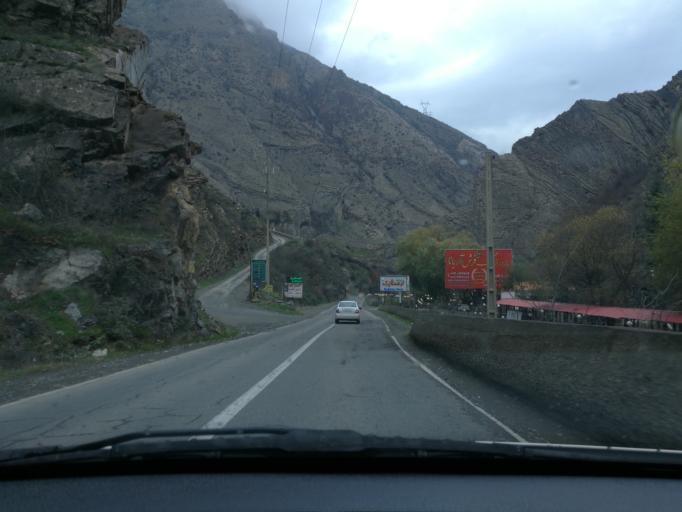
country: IR
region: Mazandaran
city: Chalus
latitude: 36.3127
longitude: 51.2480
